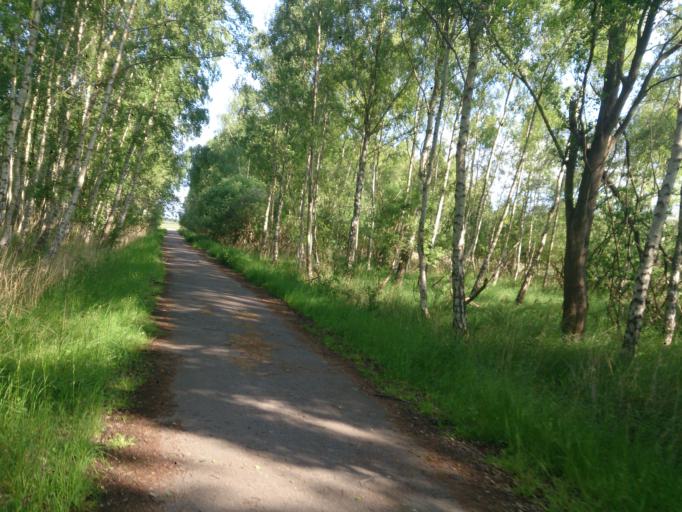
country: DK
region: Capital Region
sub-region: Tarnby Kommune
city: Tarnby
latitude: 55.5967
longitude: 12.5513
